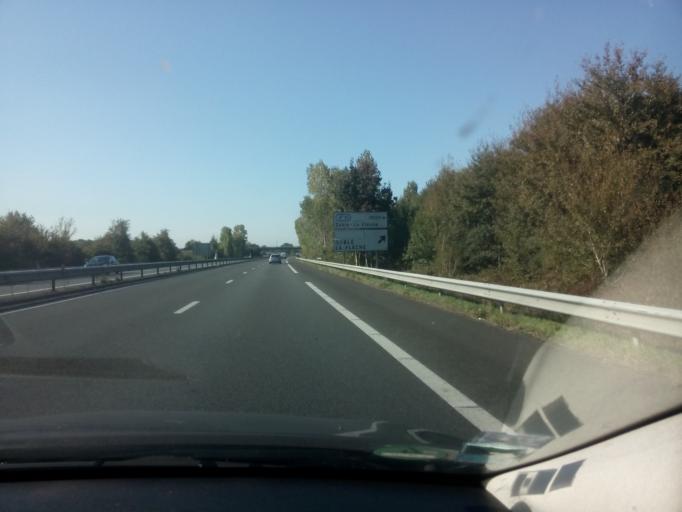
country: FR
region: Pays de la Loire
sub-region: Departement de la Sarthe
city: Parce-sur-Sarthe
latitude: 47.7863
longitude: -0.1893
